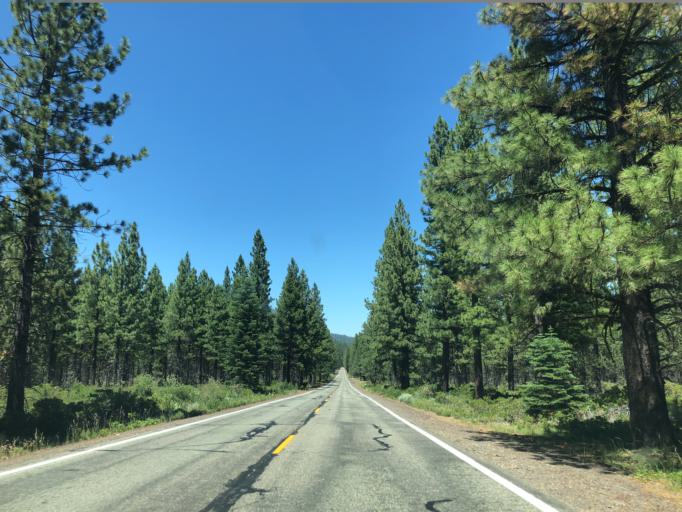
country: US
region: California
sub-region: Shasta County
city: Burney
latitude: 40.6286
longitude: -121.4778
